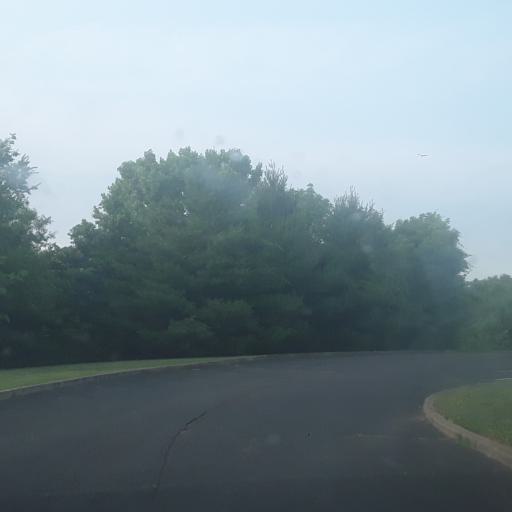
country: US
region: Tennessee
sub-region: Davidson County
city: Oak Hill
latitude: 36.0655
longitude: -86.7478
